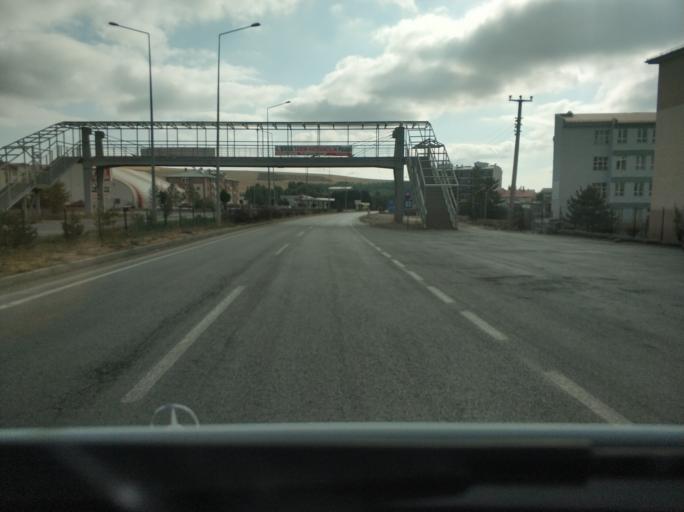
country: TR
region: Sivas
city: Yildizeli
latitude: 39.8717
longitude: 36.5996
